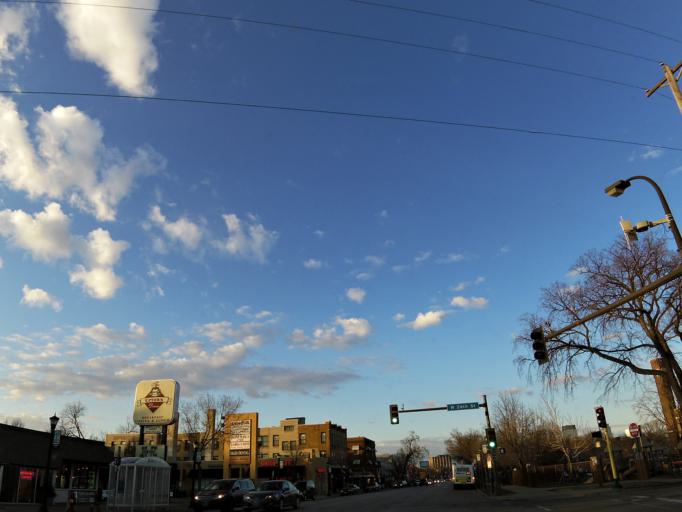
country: US
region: Minnesota
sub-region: Hennepin County
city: Minneapolis
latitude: 44.9554
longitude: -93.2969
